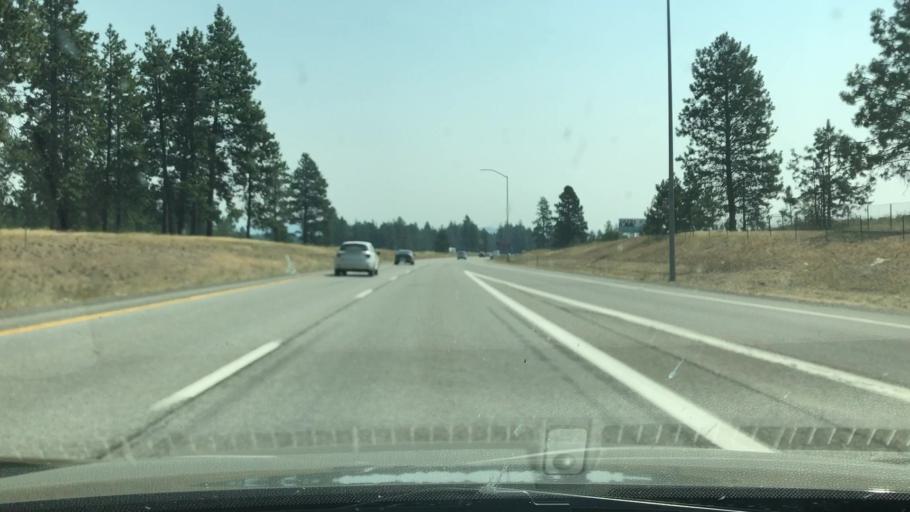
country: US
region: Idaho
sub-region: Kootenai County
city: Coeur d'Alene
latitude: 47.7083
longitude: -116.8579
